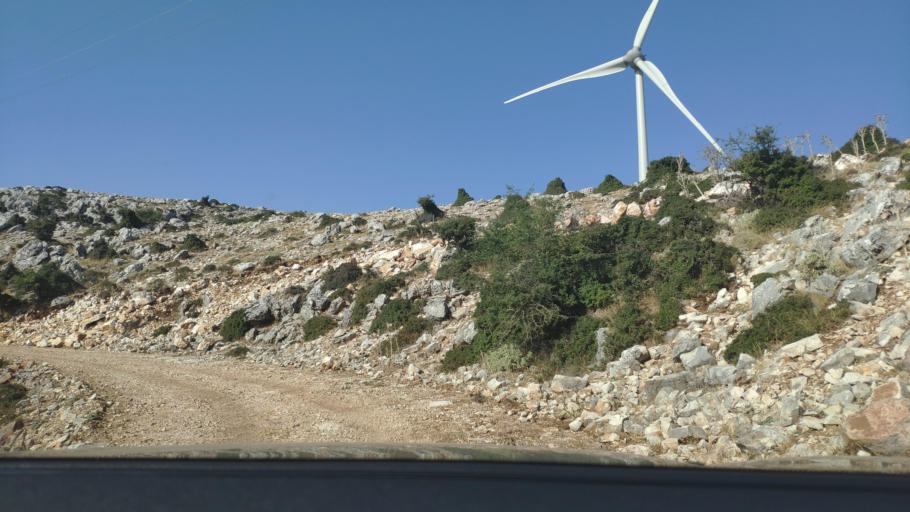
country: GR
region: West Greece
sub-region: Nomos Aitolias kai Akarnanias
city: Monastirakion
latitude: 38.8169
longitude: 20.9789
